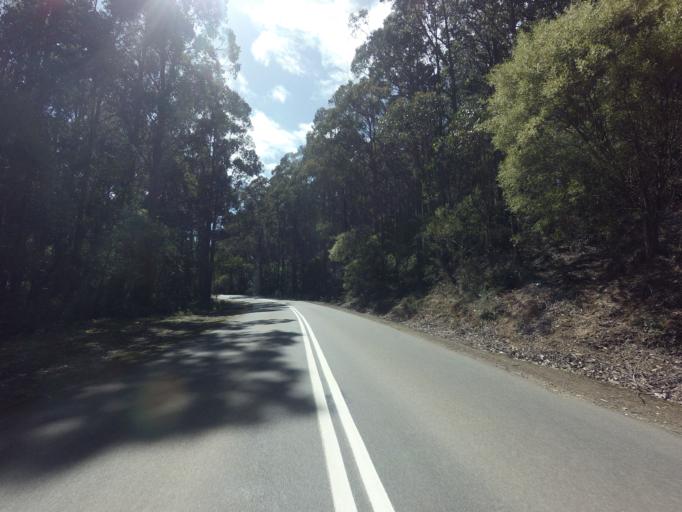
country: AU
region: Tasmania
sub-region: Derwent Valley
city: New Norfolk
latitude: -42.7302
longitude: 146.6700
